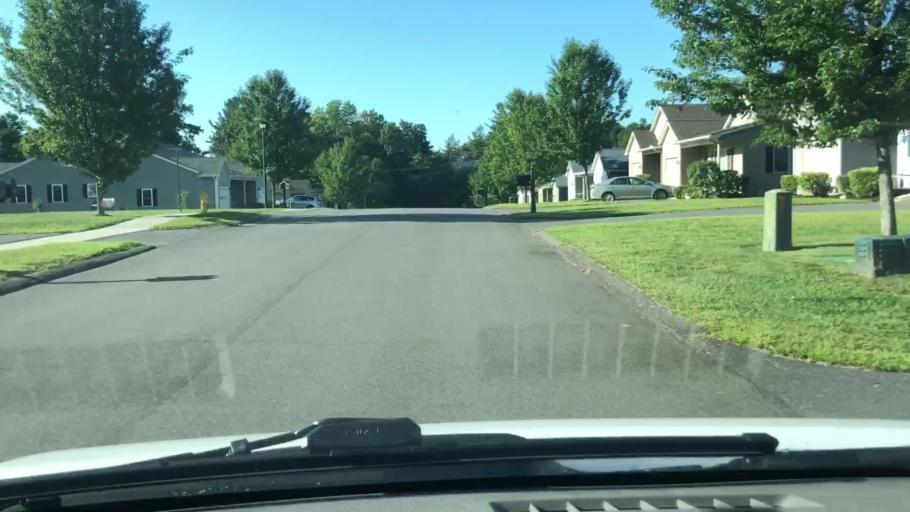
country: US
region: Massachusetts
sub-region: Franklin County
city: Greenfield
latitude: 42.6079
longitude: -72.6034
